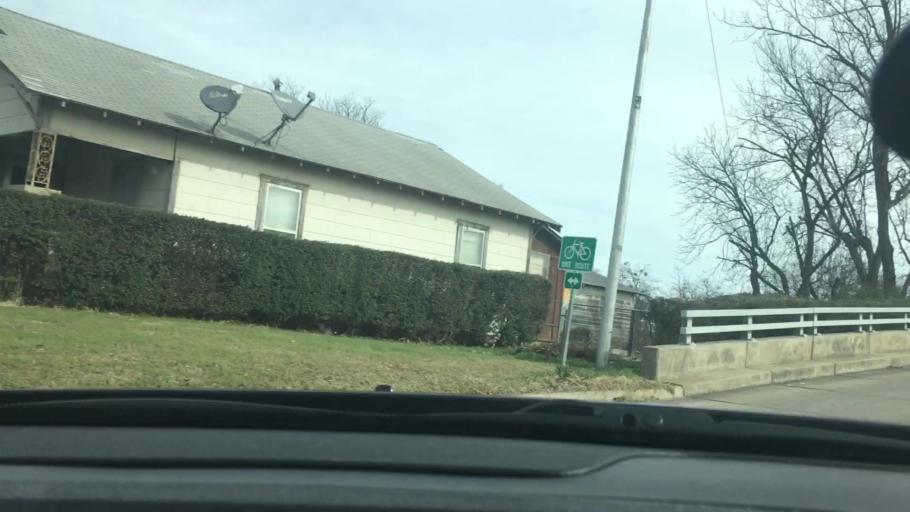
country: US
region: Oklahoma
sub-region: Carter County
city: Ardmore
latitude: 34.1776
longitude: -97.1246
